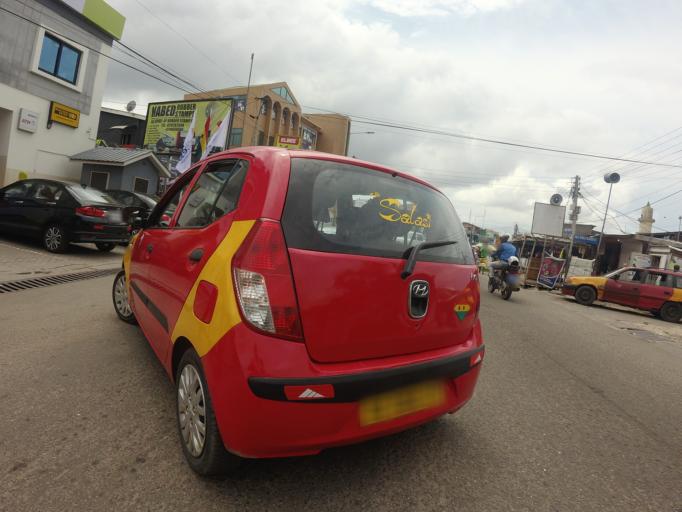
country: GH
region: Greater Accra
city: Accra
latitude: 5.5826
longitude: -0.2085
